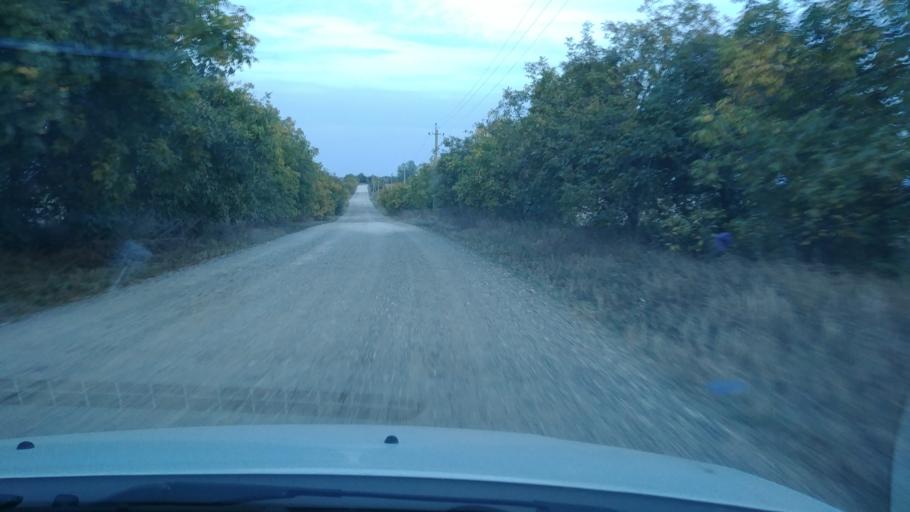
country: MD
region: Rezina
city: Saharna
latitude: 47.6813
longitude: 28.9085
